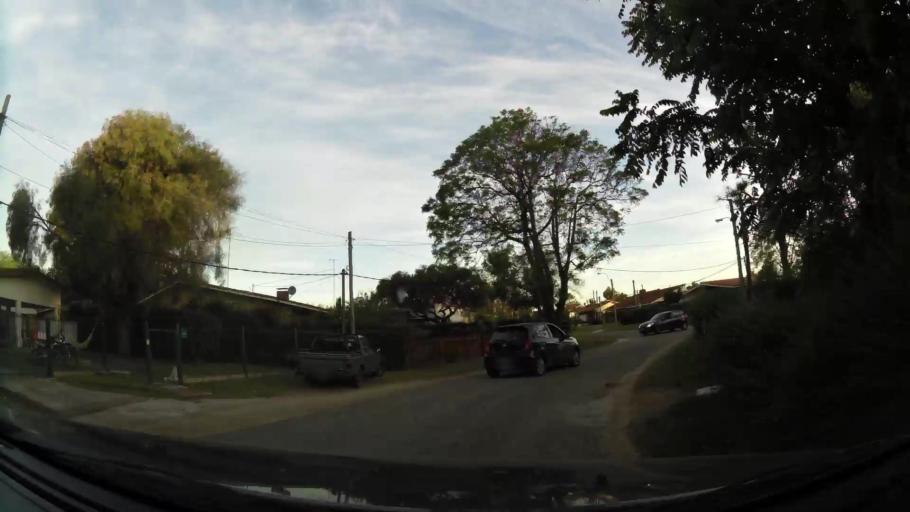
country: UY
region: Canelones
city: Atlantida
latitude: -34.7691
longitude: -55.7762
